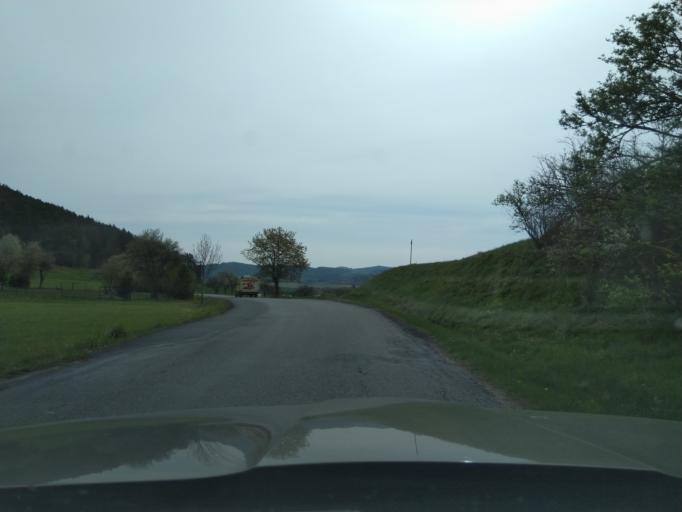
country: CZ
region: Plzensky
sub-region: Okres Klatovy
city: Susice
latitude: 49.2287
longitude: 13.5846
